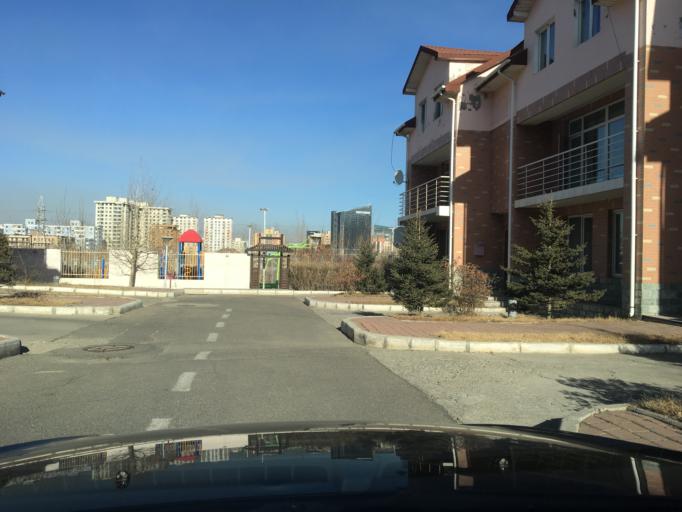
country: MN
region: Ulaanbaatar
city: Ulaanbaatar
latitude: 47.8884
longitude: 106.9086
